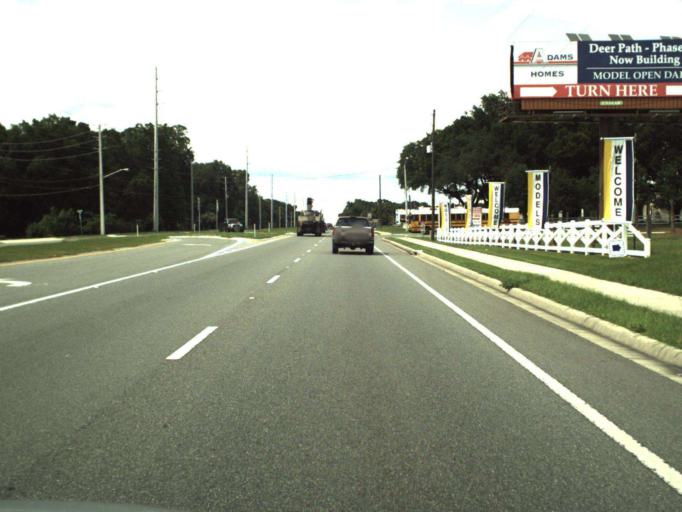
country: US
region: Florida
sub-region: Marion County
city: Silver Springs Shores
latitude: 29.1780
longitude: -82.0535
